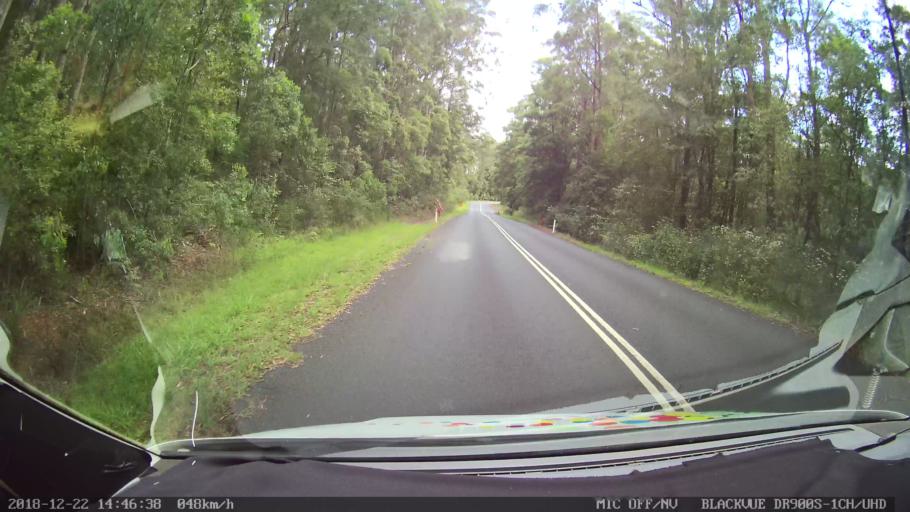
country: AU
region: New South Wales
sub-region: Bellingen
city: Dorrigo
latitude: -30.1735
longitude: 152.5607
